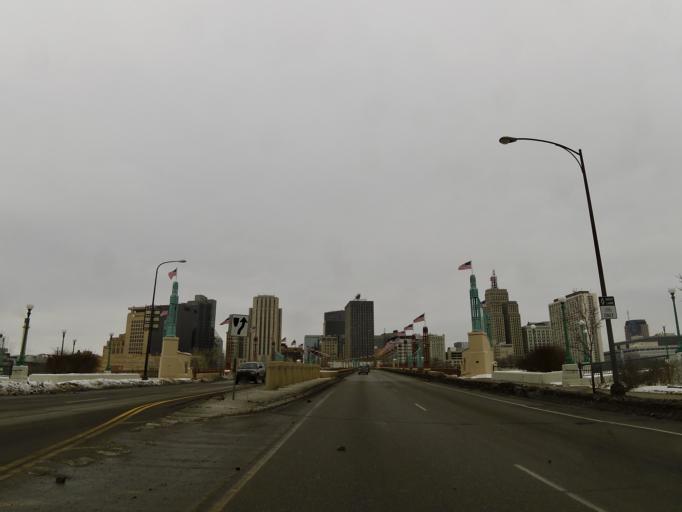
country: US
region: Minnesota
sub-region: Ramsey County
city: Saint Paul
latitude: 44.9403
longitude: -93.0901
